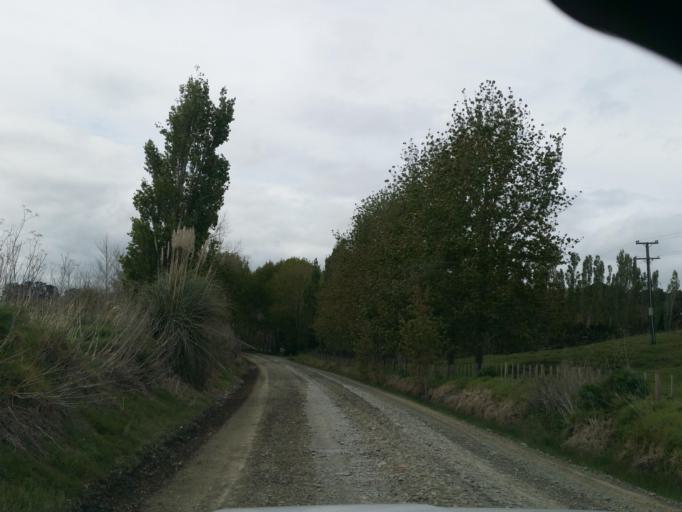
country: NZ
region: Northland
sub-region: Kaipara District
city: Dargaville
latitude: -35.9240
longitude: 173.9219
